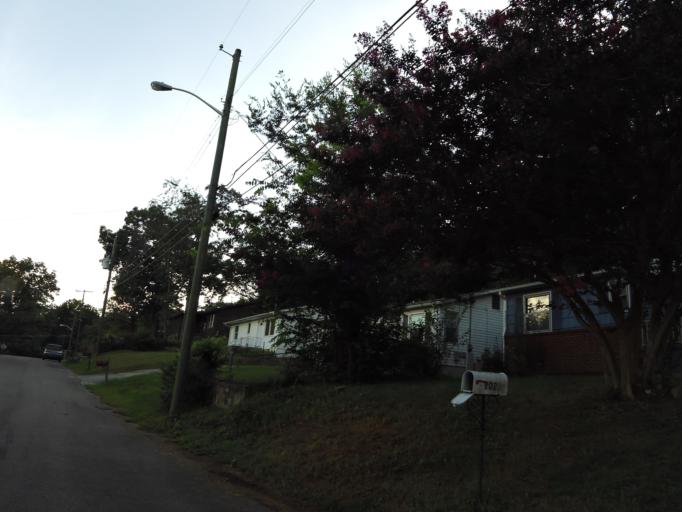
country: US
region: Tennessee
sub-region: Knox County
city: Knoxville
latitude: 36.0072
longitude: -83.9332
